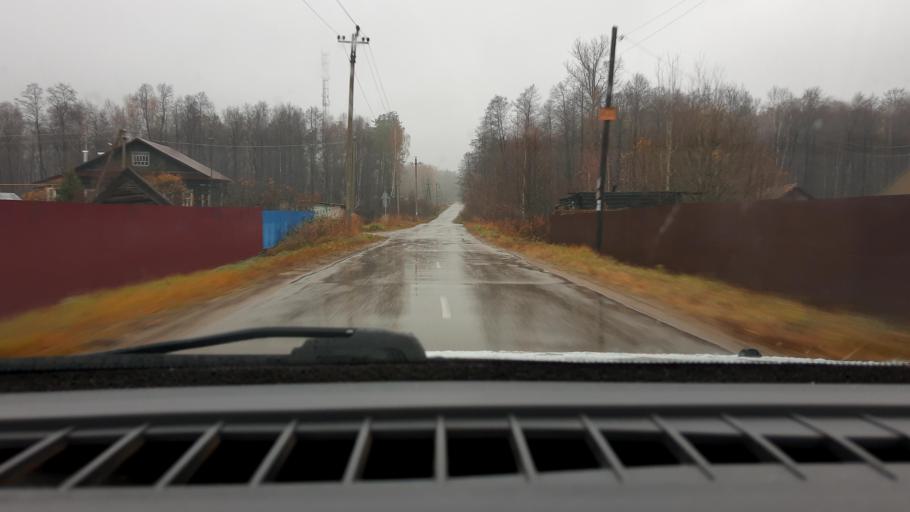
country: RU
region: Nizjnij Novgorod
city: Linda
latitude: 56.6868
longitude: 44.2023
